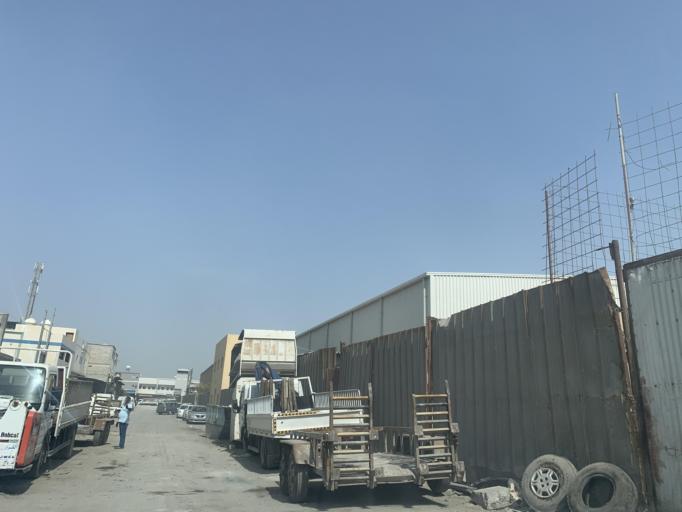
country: BH
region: Central Governorate
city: Madinat Hamad
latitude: 26.1383
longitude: 50.4813
